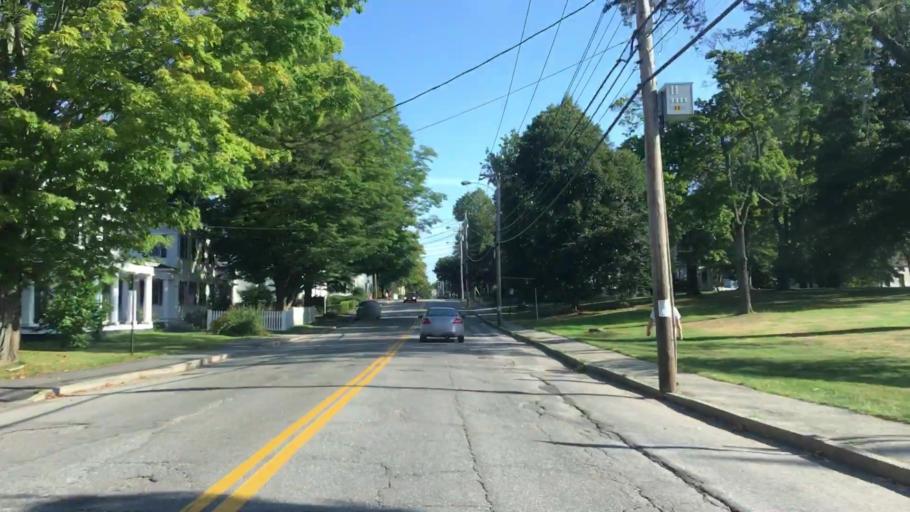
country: US
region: Maine
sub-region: Sagadahoc County
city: Bath
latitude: 43.9158
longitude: -69.8162
